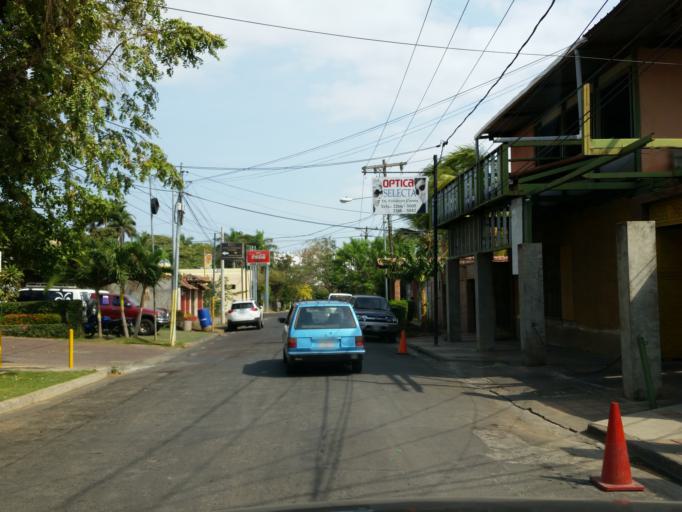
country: NI
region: Managua
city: Managua
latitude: 12.1376
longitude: -86.2811
